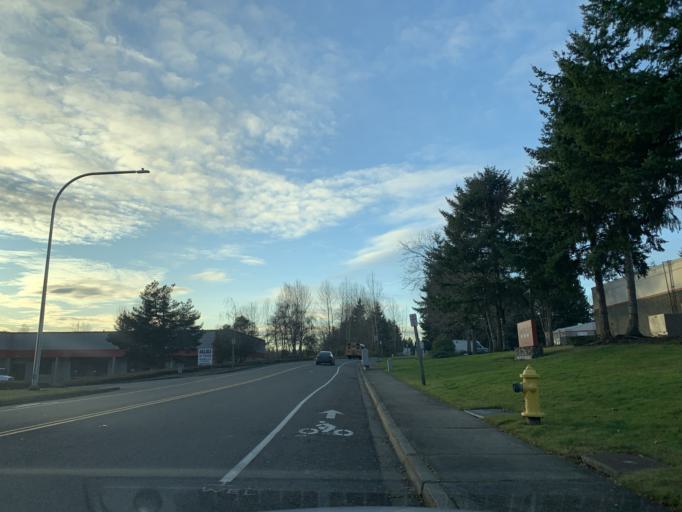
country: US
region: Washington
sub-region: King County
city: Federal Way
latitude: 47.2937
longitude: -122.3199
